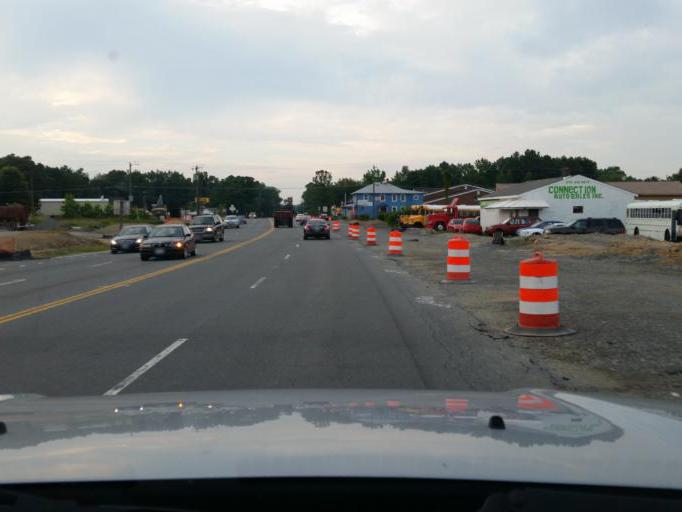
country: US
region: Virginia
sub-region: Spotsylvania County
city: Spotsylvania Courthouse
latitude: 38.1338
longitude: -77.5215
